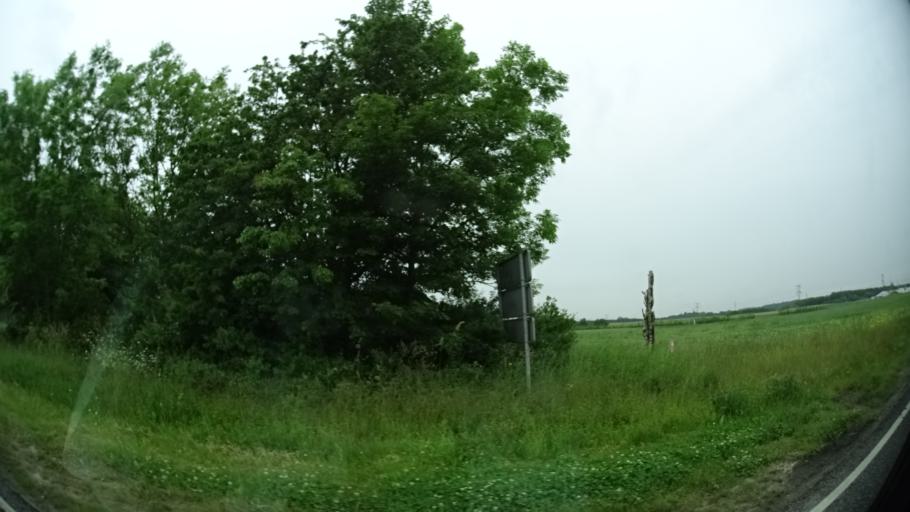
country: DK
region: Central Jutland
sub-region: Arhus Kommune
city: Logten
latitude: 56.2462
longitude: 10.3008
